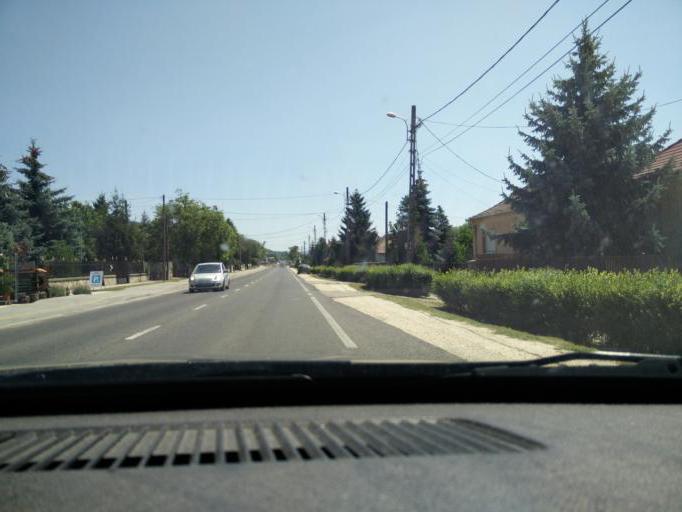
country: HU
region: Komarom-Esztergom
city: Vertesszolos
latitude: 47.6160
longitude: 18.3797
